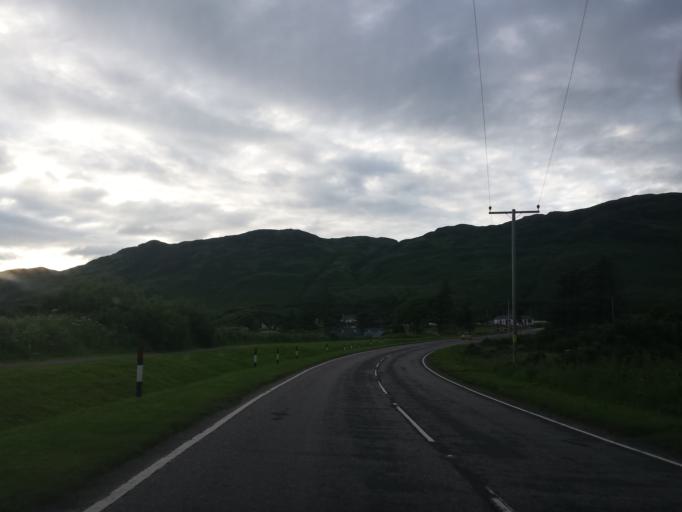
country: GB
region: Scotland
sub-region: Highland
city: Fort William
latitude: 57.2794
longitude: -5.5216
